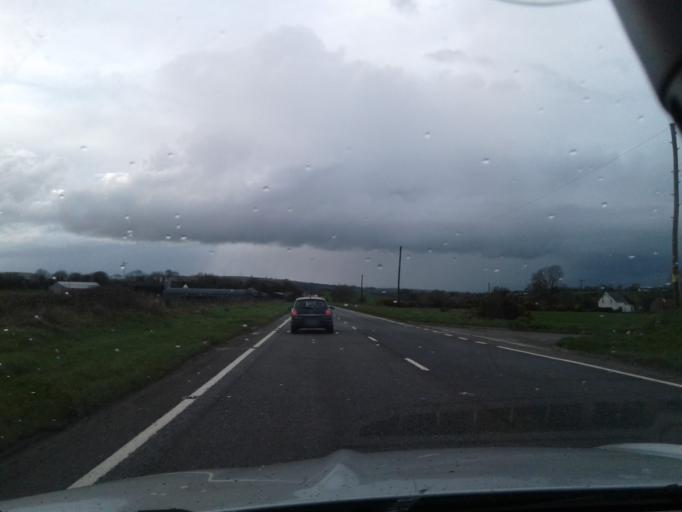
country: GB
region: Northern Ireland
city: Newtownstewart
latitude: 54.7292
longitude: -7.4116
